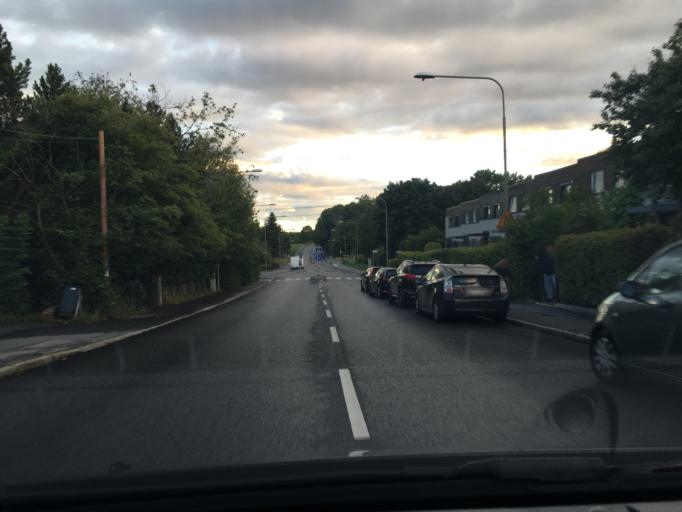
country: SE
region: Stockholm
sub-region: Jarfalla Kommun
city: Jakobsberg
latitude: 59.3756
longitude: 17.8722
